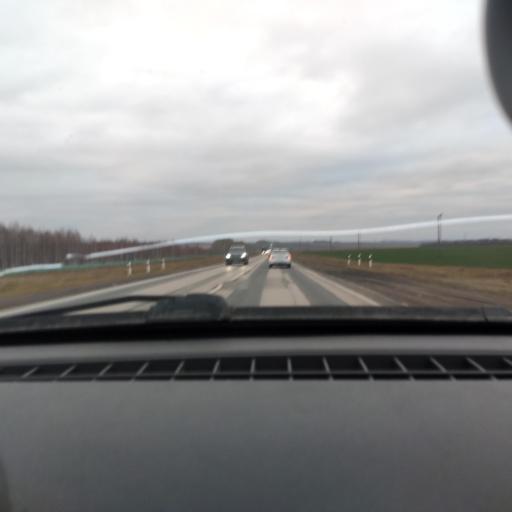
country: RU
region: Bashkortostan
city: Karmaskaly
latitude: 54.4266
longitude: 56.0305
